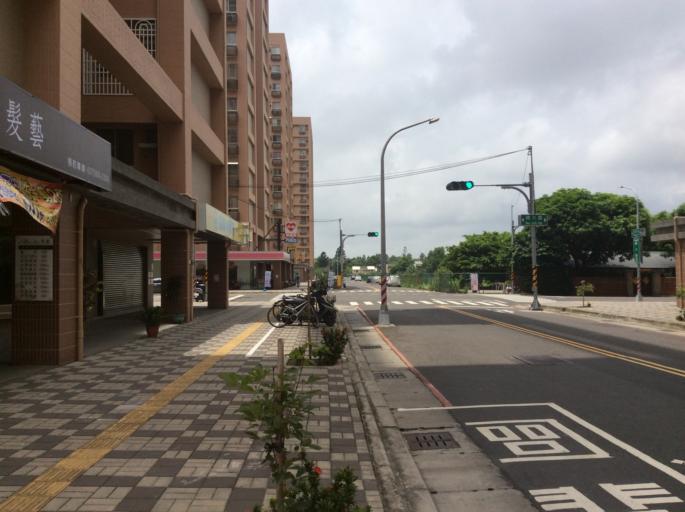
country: TW
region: Kaohsiung
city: Kaohsiung
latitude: 22.6970
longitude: 120.2875
